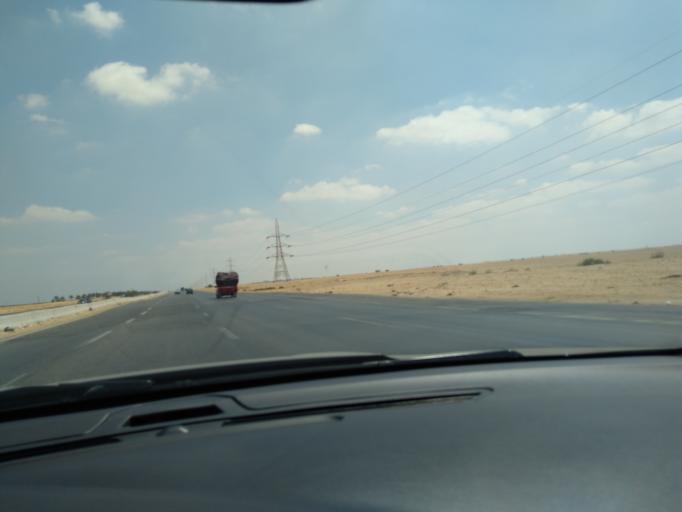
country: EG
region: Al Isma'iliyah
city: At Tall al Kabir
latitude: 30.3760
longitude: 31.9361
